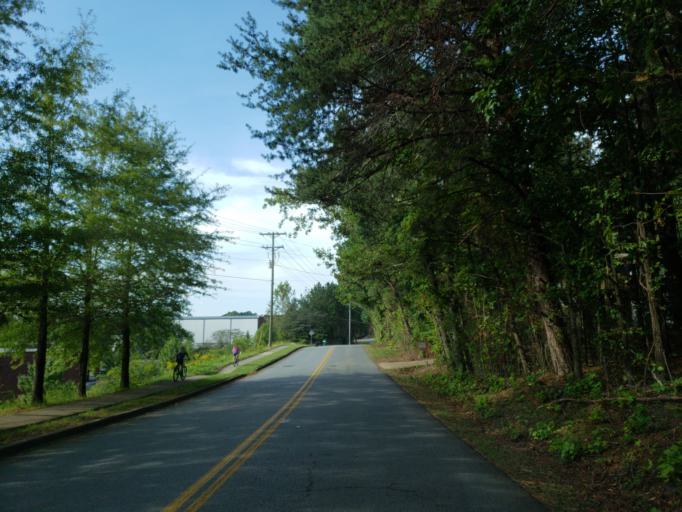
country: US
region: Georgia
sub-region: Cherokee County
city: Woodstock
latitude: 34.0832
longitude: -84.4981
